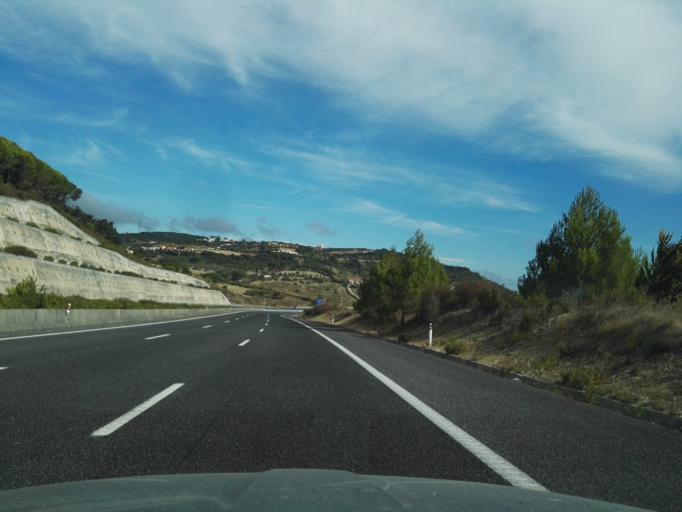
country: PT
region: Lisbon
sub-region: Arruda Dos Vinhos
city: Arruda dos Vinhos
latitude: 38.9457
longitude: -9.0666
